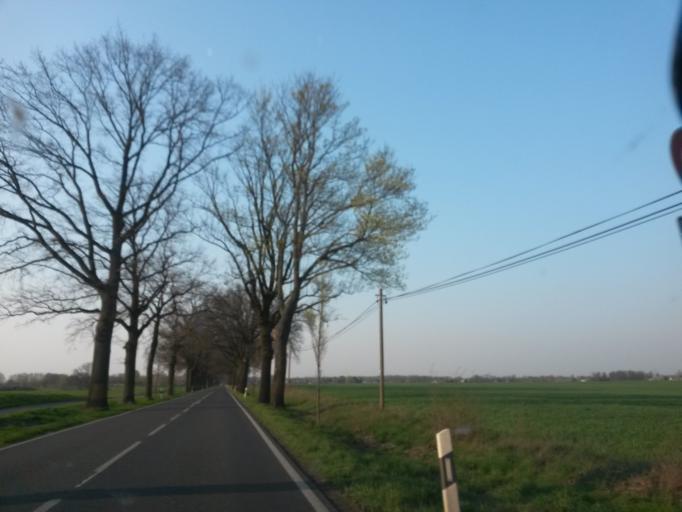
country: DE
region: Brandenburg
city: Rehfelde
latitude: 52.5114
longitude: 13.9306
